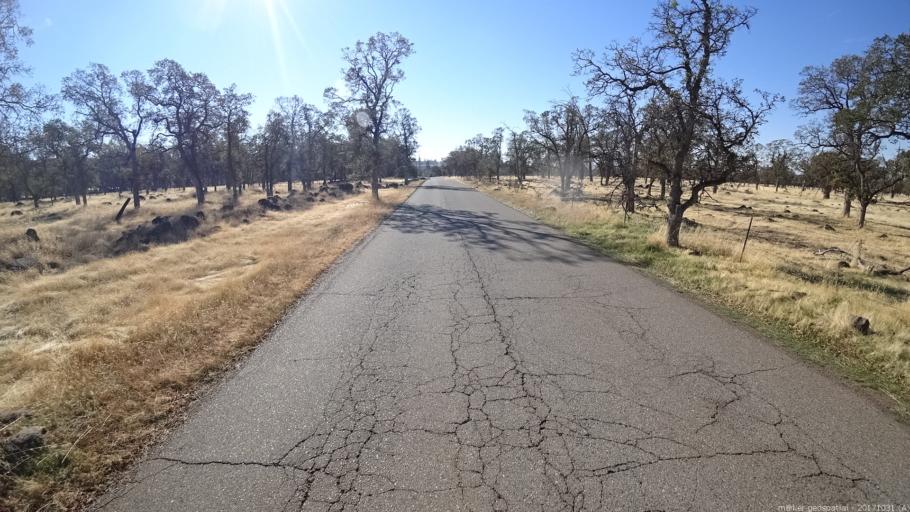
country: US
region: California
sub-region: Shasta County
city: Shingletown
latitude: 40.4415
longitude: -121.8713
